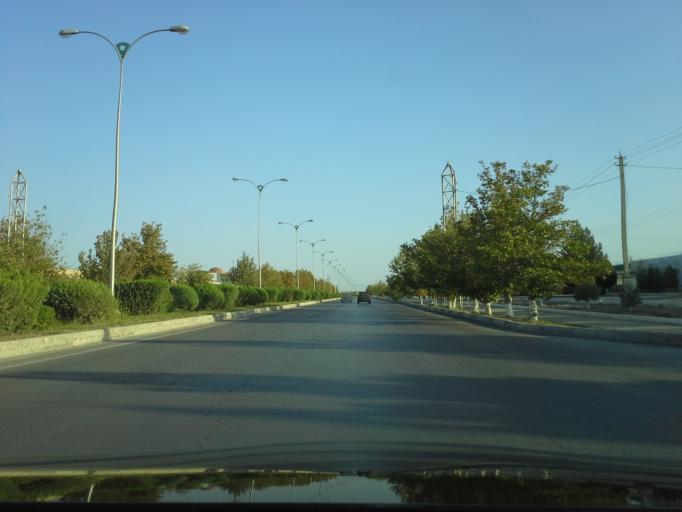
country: TM
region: Ahal
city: Abadan
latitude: 38.0298
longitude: 58.1944
